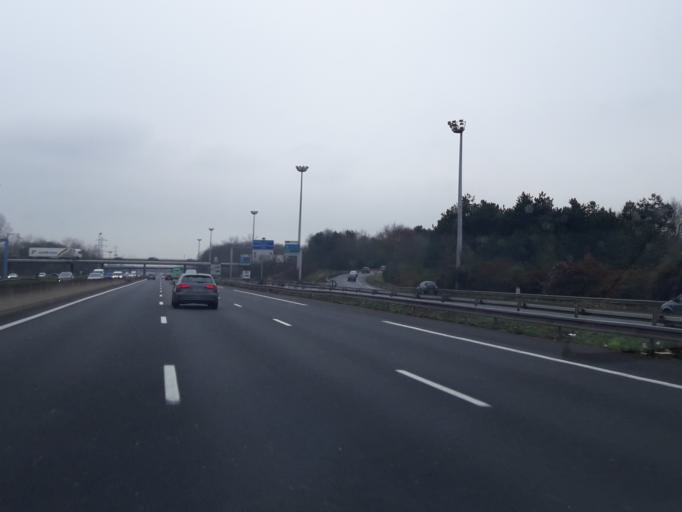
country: FR
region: Ile-de-France
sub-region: Departement de l'Essonne
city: Grigny
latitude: 48.6369
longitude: 2.3986
